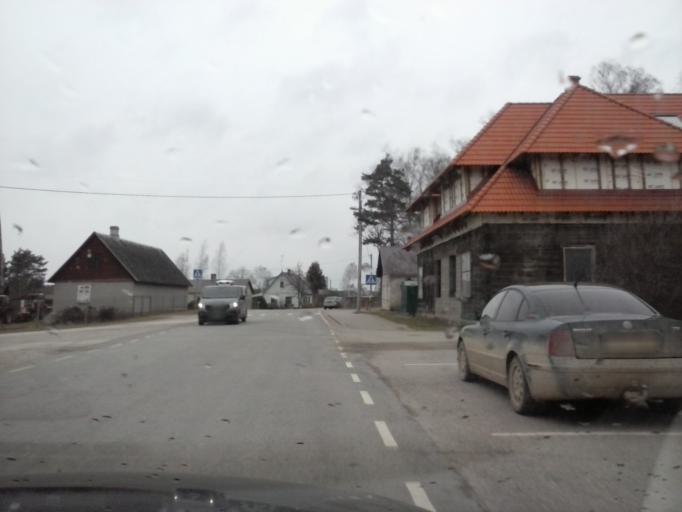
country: RU
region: Pskov
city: Pechory
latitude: 57.9591
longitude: 27.6307
